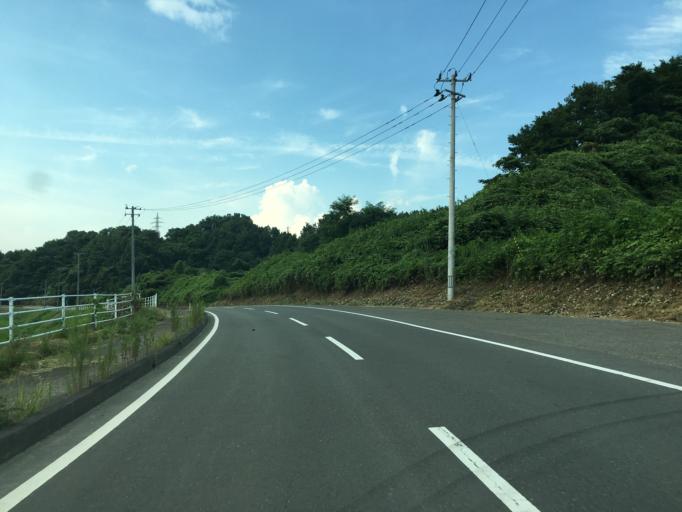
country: JP
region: Fukushima
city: Nihommatsu
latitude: 37.5476
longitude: 140.4418
